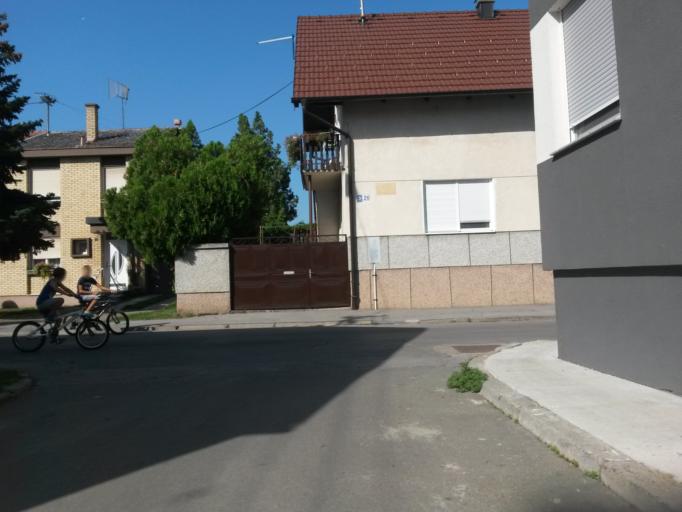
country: HR
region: Osjecko-Baranjska
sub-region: Grad Osijek
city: Osijek
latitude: 45.5469
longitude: 18.6986
